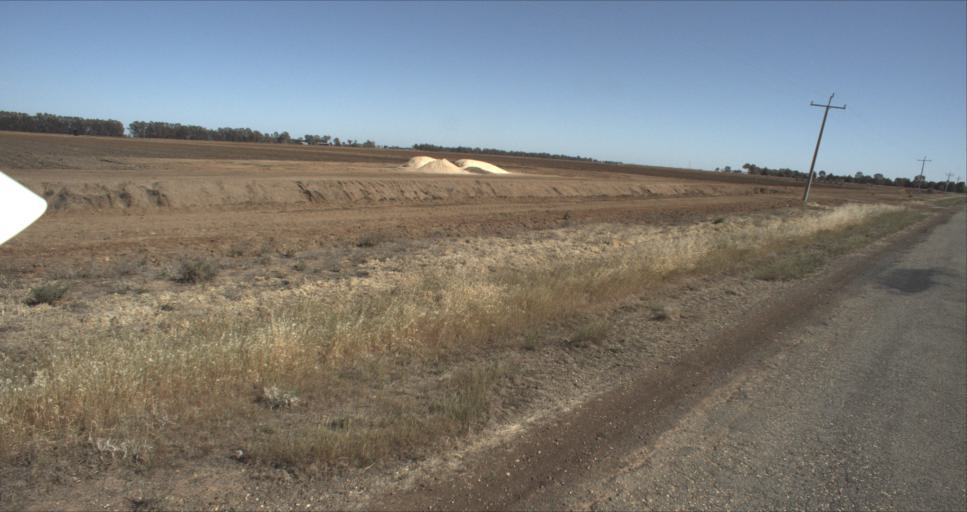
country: AU
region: New South Wales
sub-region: Leeton
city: Leeton
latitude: -34.5950
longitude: 146.2589
